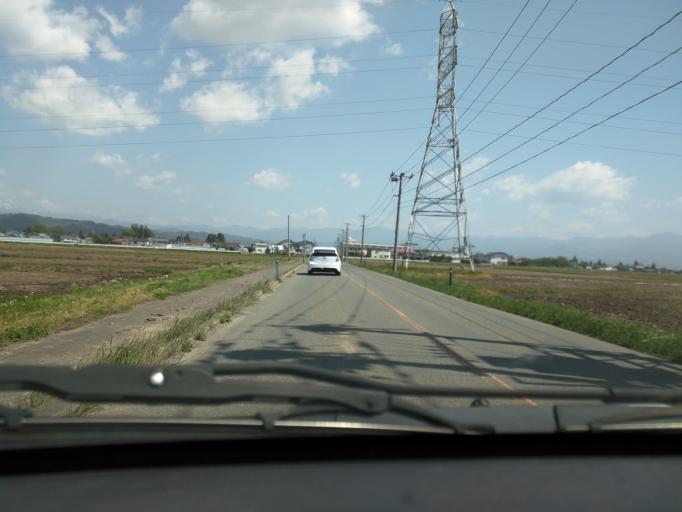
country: JP
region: Fukushima
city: Kitakata
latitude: 37.5829
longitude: 139.8343
